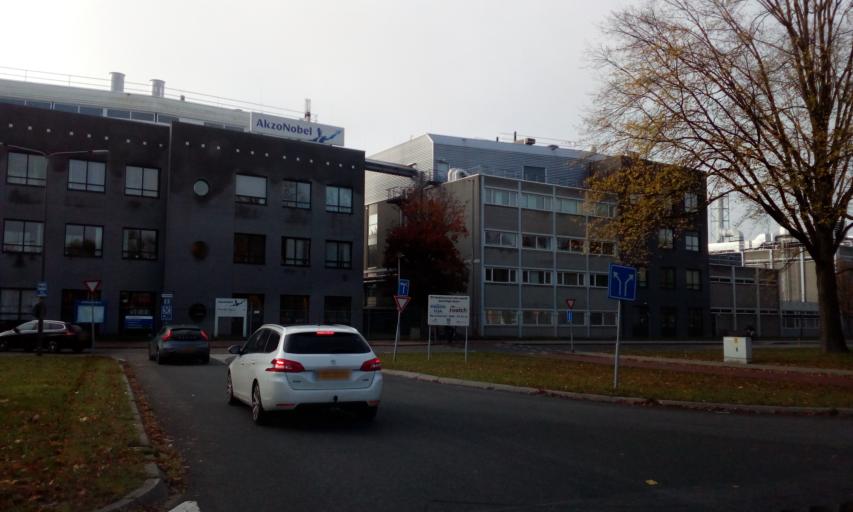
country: NL
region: Overijssel
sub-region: Gemeente Deventer
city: Deventer
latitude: 52.2391
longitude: 6.1768
